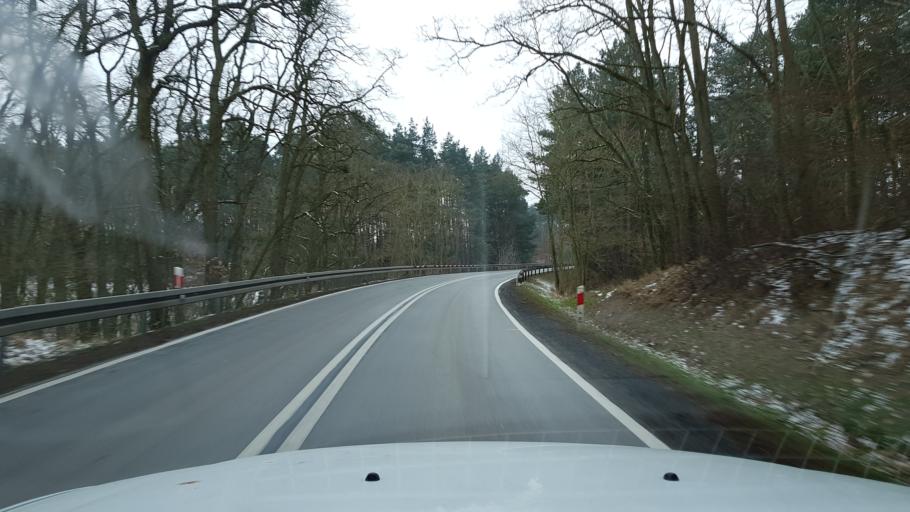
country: PL
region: West Pomeranian Voivodeship
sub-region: Powiat gryfinski
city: Widuchowa
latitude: 53.1336
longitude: 14.4077
